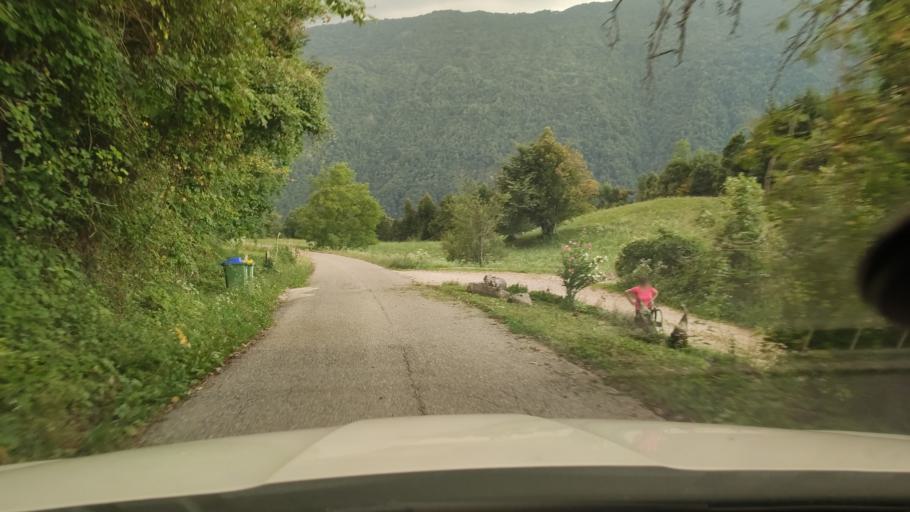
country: IT
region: Friuli Venezia Giulia
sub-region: Provincia di Udine
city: Cras
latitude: 46.2212
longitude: 13.6398
